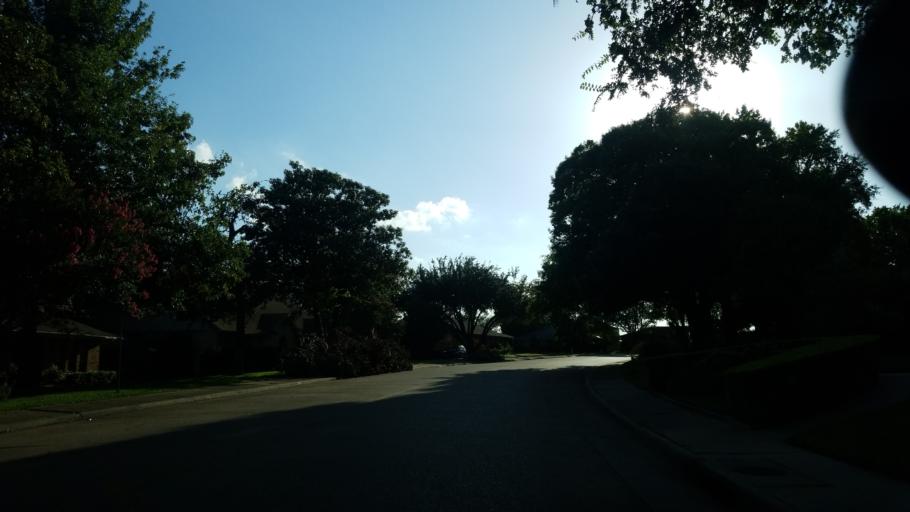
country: US
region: Texas
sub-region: Dallas County
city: Highland Park
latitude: 32.7863
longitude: -96.7114
